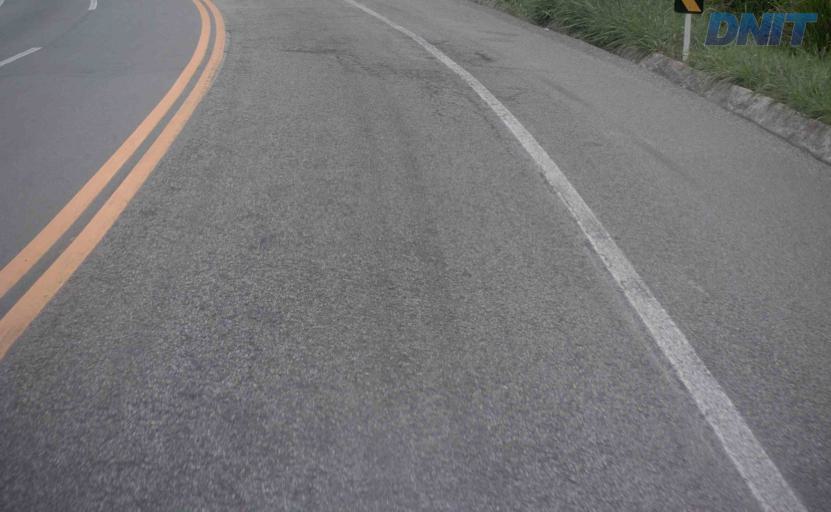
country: BR
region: Minas Gerais
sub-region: Nova Era
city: Nova Era
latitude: -19.6891
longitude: -42.9909
